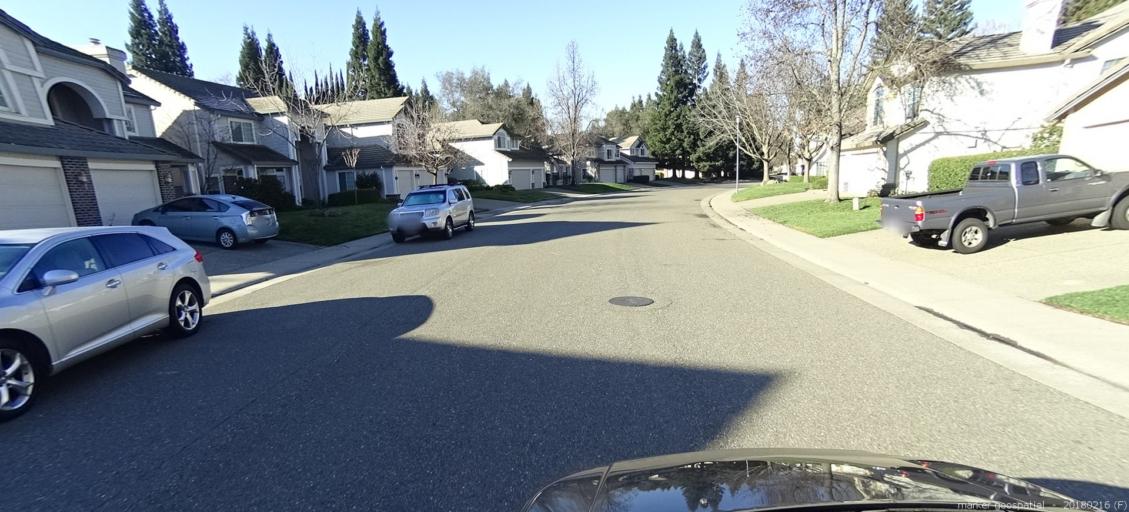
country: US
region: California
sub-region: Sacramento County
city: Gold River
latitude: 38.6271
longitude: -121.2318
